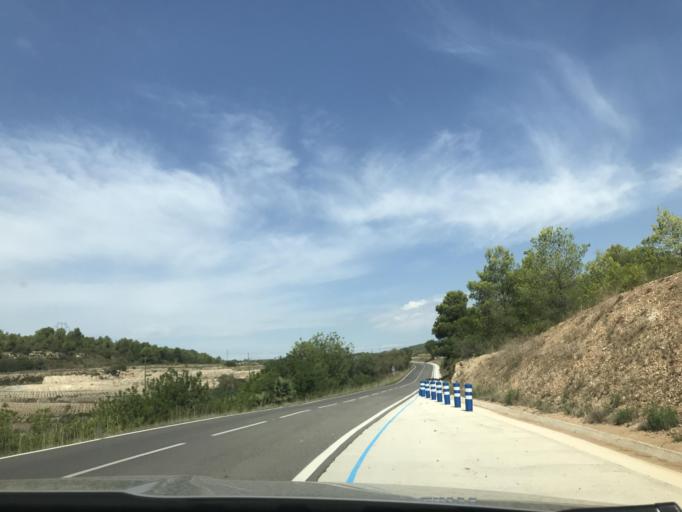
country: ES
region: Catalonia
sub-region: Provincia de Tarragona
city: Salomo
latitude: 41.2184
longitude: 1.3801
